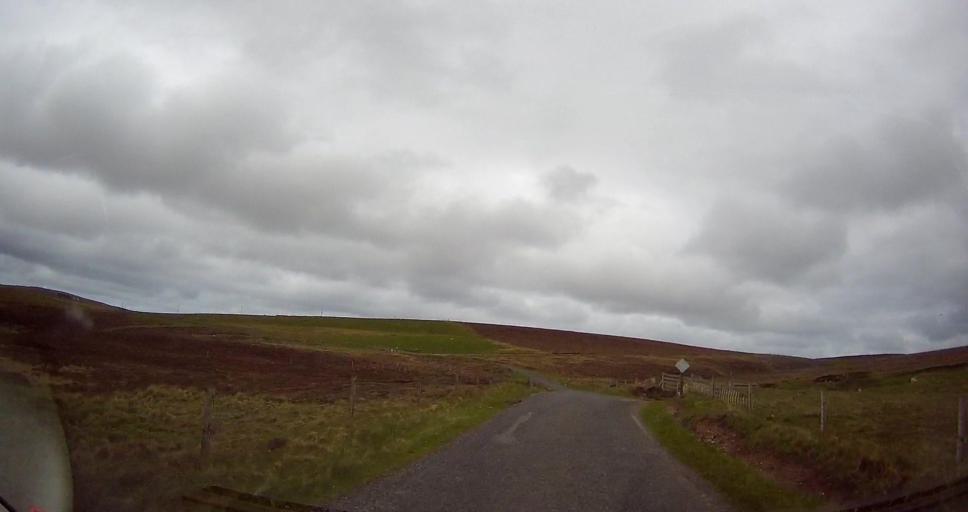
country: GB
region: Scotland
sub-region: Shetland Islands
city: Shetland
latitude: 60.7970
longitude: -0.8593
